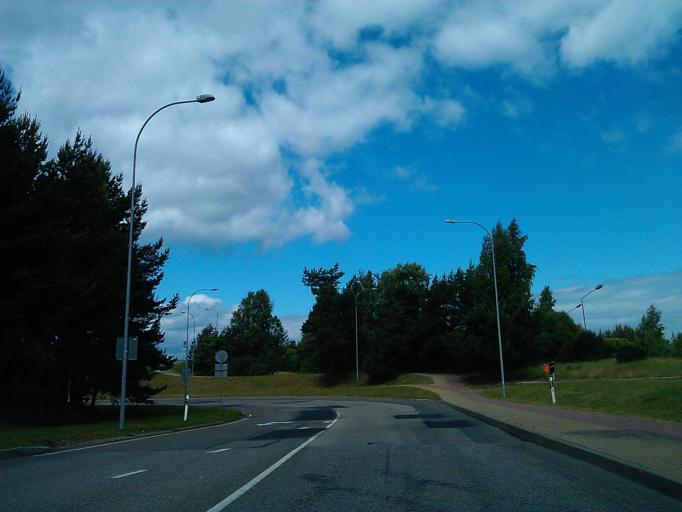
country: LV
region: Babite
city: Pinki
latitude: 56.9704
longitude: 23.8671
